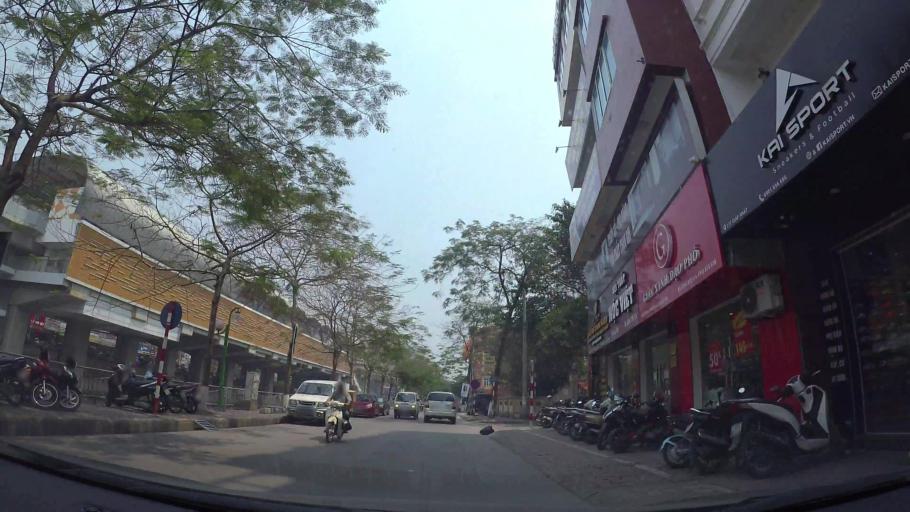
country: VN
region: Ha Noi
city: Thanh Xuan
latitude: 21.0068
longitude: 105.8152
